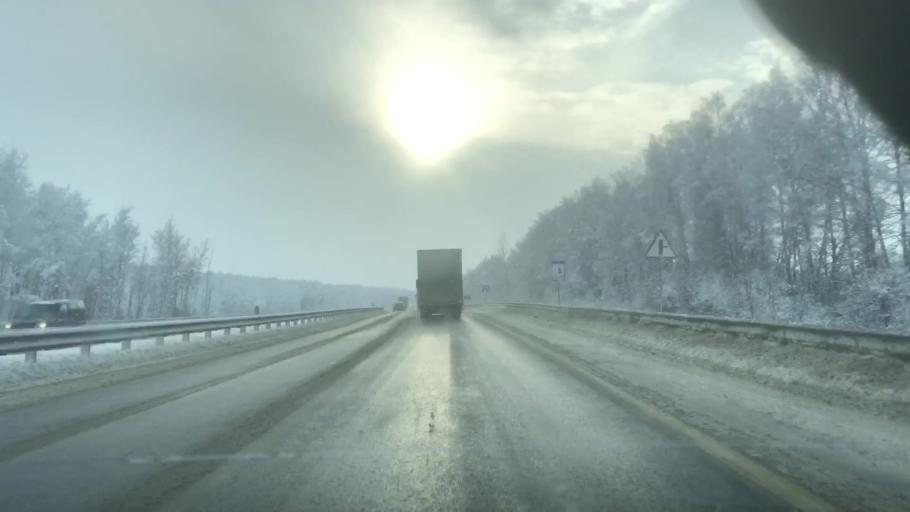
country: RU
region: Tula
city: Venev
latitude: 54.5193
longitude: 38.1693
